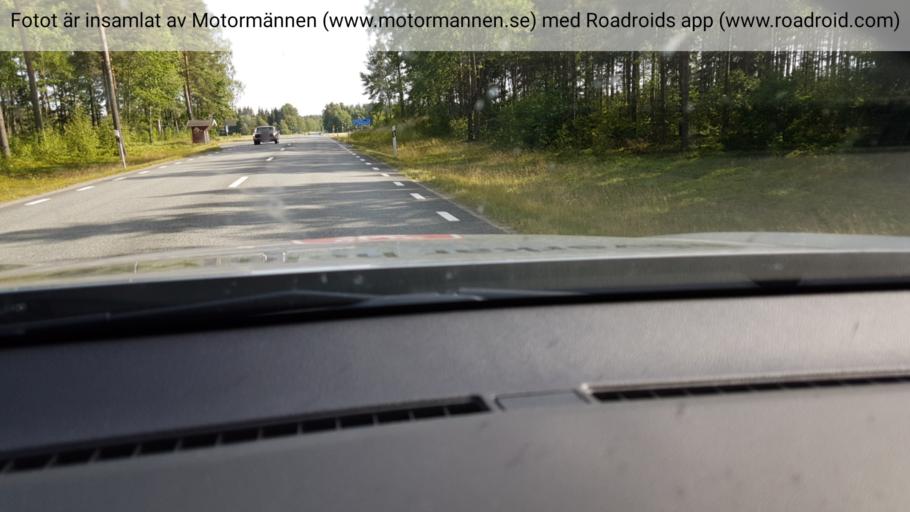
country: SE
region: Joenkoeping
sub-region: Eksjo Kommun
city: Eksjoe
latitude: 57.6041
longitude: 14.9695
